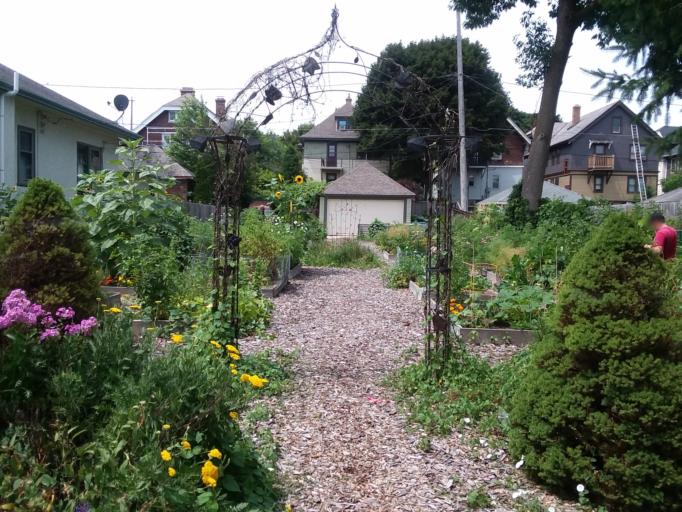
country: US
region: Wisconsin
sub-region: Milwaukee County
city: Wauwatosa
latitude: 43.0575
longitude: -87.9749
